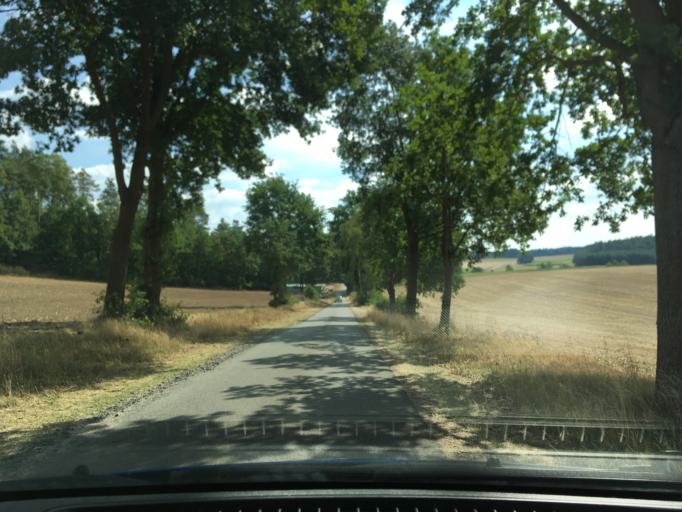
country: DE
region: Lower Saxony
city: Gohrde
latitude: 53.1219
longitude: 10.9454
